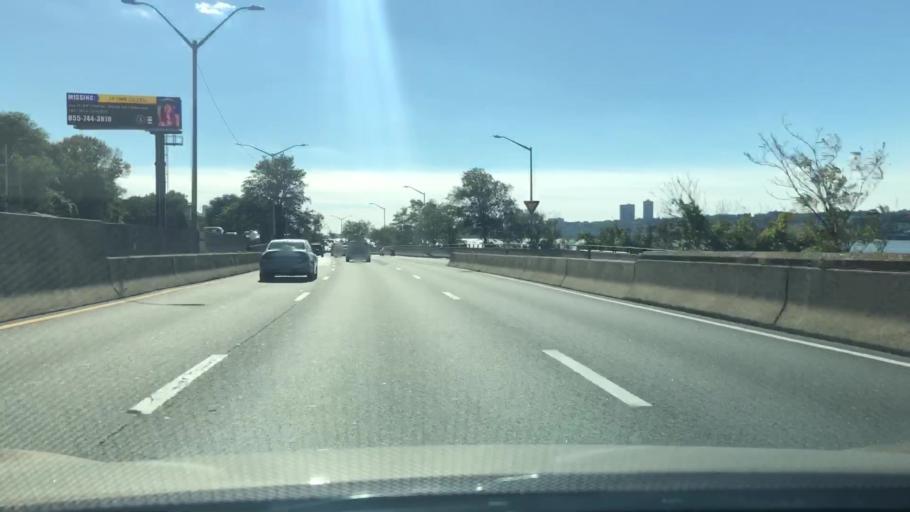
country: US
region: New Jersey
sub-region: Bergen County
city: Edgewater
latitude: 40.8168
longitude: -73.9630
